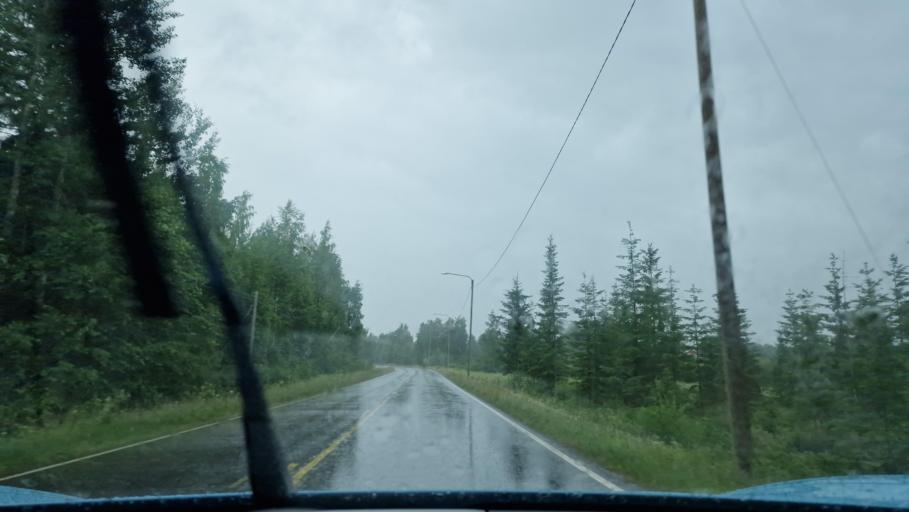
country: FI
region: Southern Ostrobothnia
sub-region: Jaerviseutu
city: Soini
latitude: 62.8404
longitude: 24.3293
